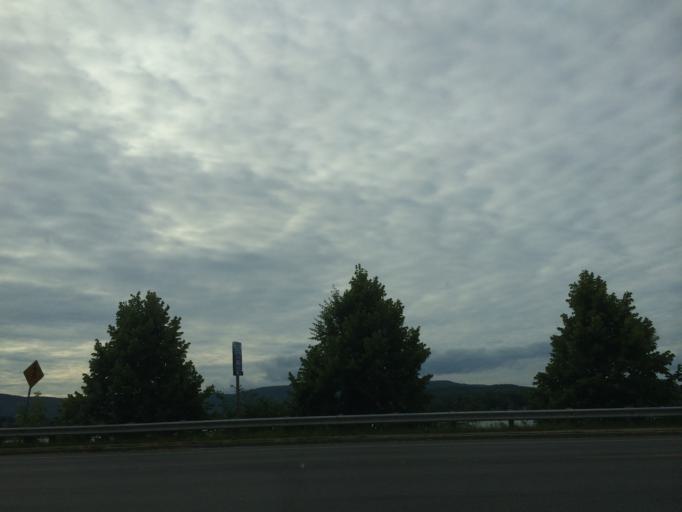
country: US
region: Massachusetts
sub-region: Berkshire County
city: Lanesborough
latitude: 42.4923
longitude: -73.2424
